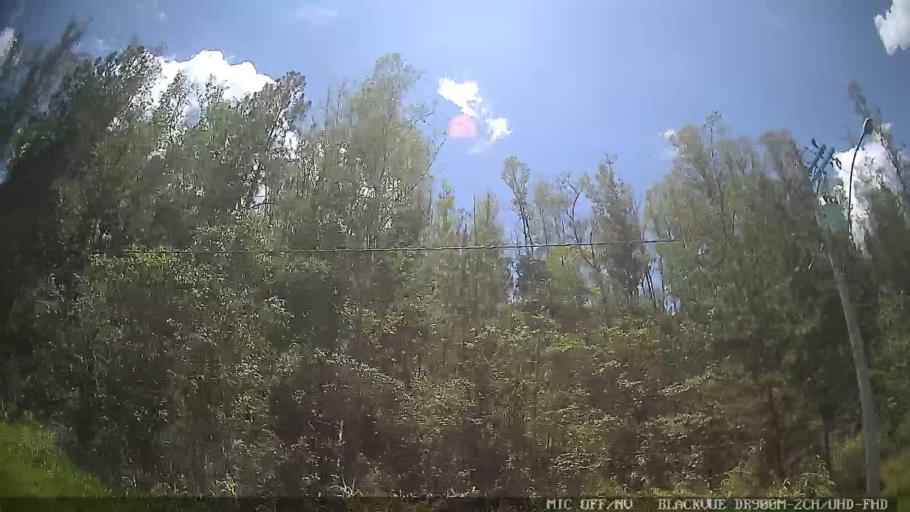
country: BR
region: Sao Paulo
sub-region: Amparo
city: Amparo
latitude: -22.6949
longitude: -46.7560
